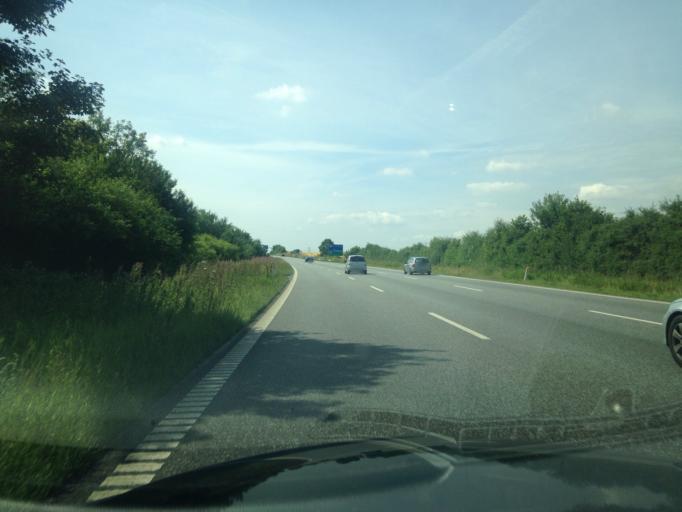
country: DK
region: South Denmark
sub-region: Kolding Kommune
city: Kolding
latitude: 55.5441
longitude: 9.5189
